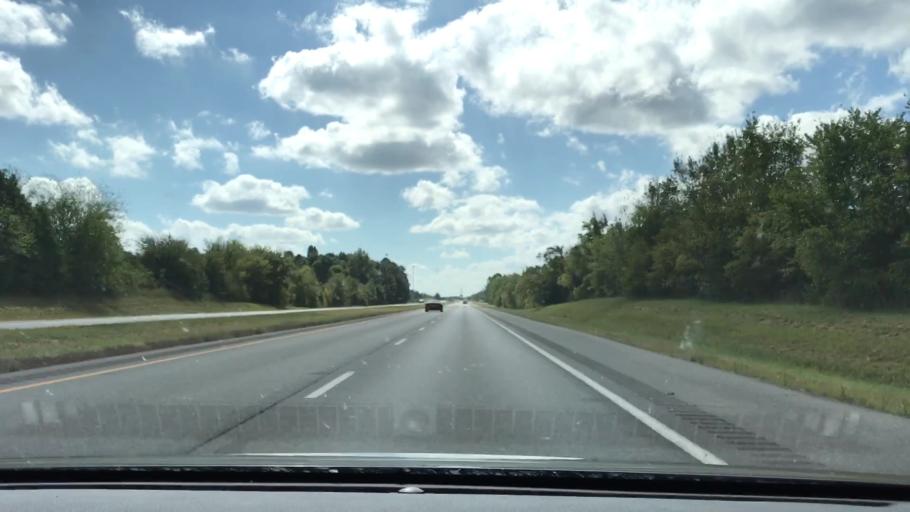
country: US
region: Kentucky
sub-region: McCracken County
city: Reidland
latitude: 37.0012
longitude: -88.5068
